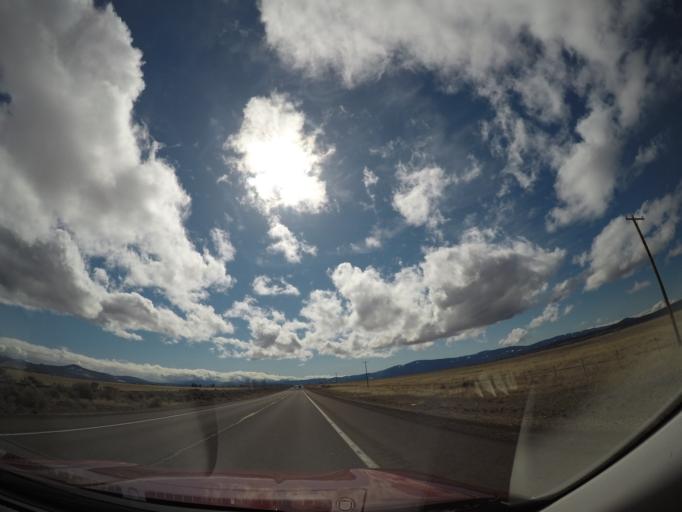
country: US
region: Oregon
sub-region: Klamath County
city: Klamath Falls
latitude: 41.9443
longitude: -121.9305
